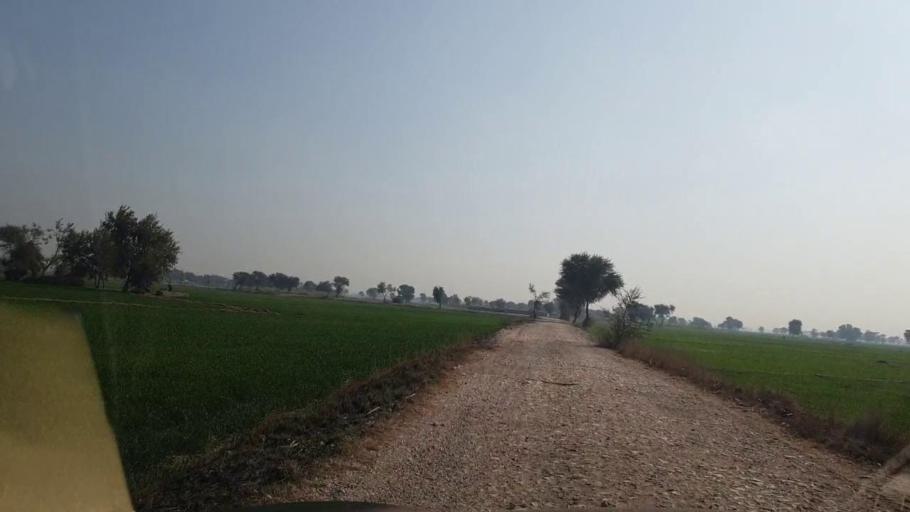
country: PK
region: Sindh
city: Ubauro
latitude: 28.1137
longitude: 69.7893
